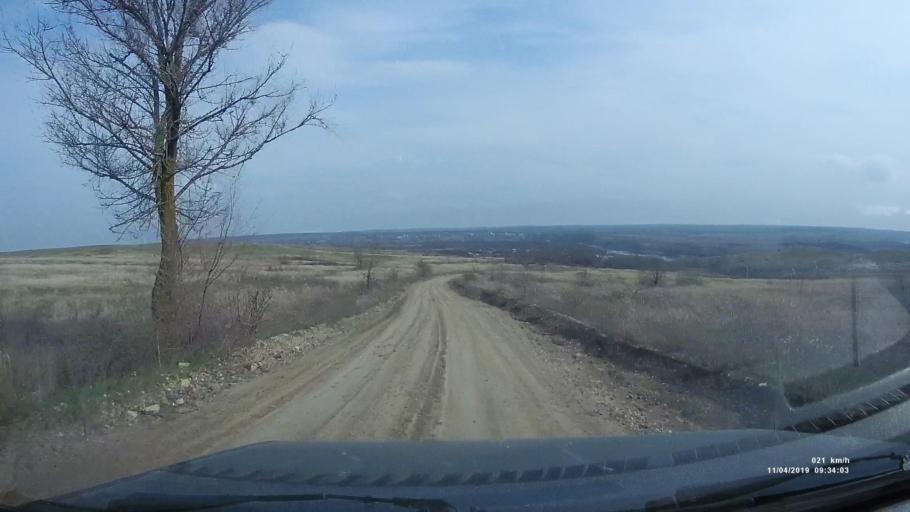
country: RU
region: Rostov
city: Staraya Stanitsa
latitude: 48.2679
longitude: 40.3686
